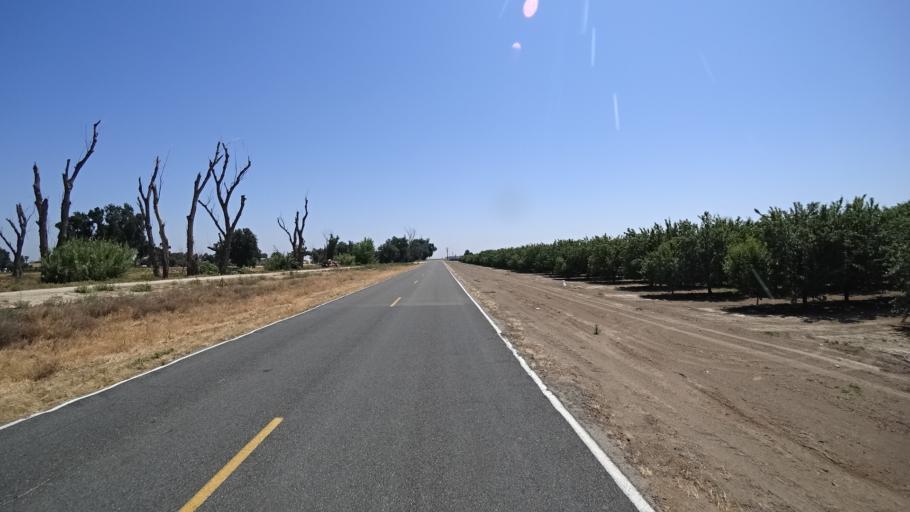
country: US
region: California
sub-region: Kings County
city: Lemoore
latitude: 36.3708
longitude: -119.7948
